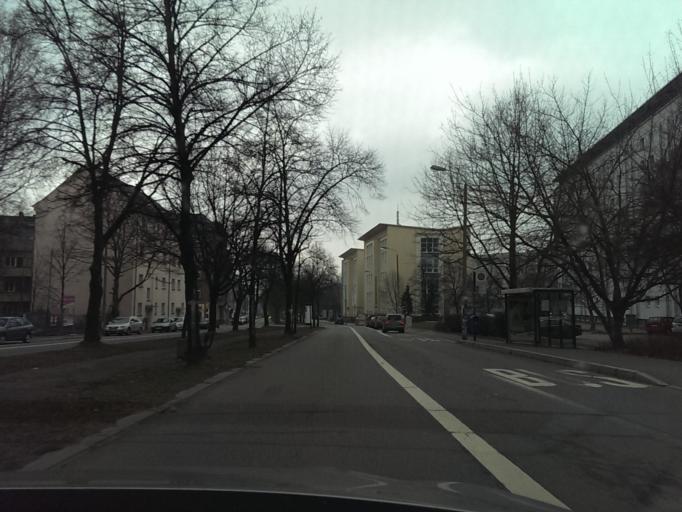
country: DE
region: Saxony
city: Chemnitz
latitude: 50.8173
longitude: 12.9297
